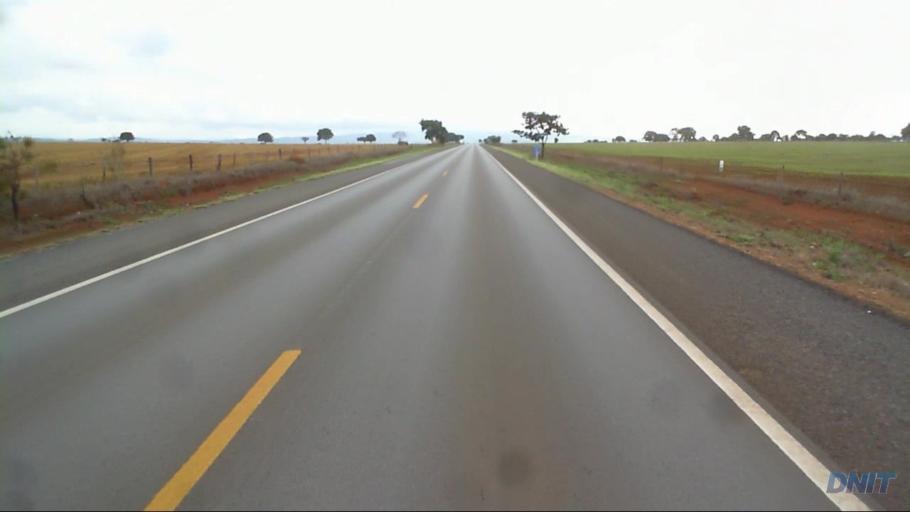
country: BR
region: Goias
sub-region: Padre Bernardo
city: Padre Bernardo
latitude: -15.2178
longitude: -48.6167
